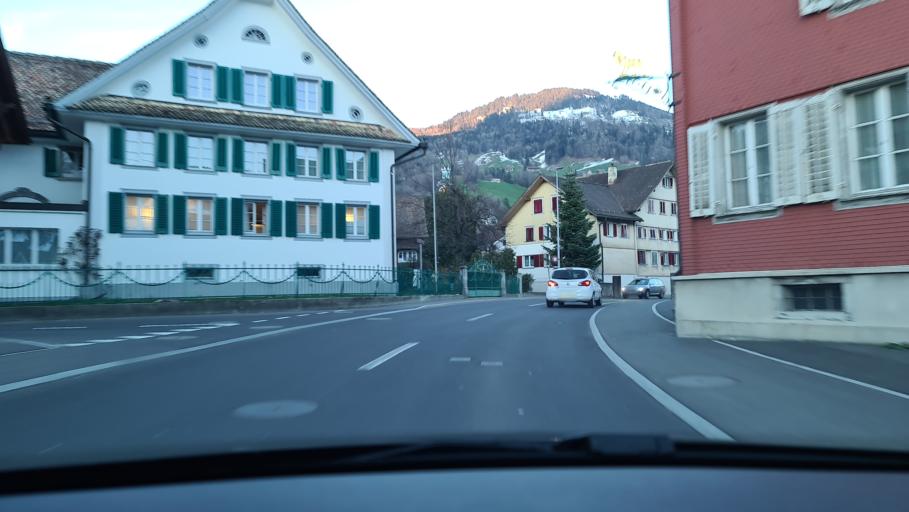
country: CH
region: Schwyz
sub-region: Bezirk Schwyz
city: Steinen
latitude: 47.0493
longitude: 8.6111
